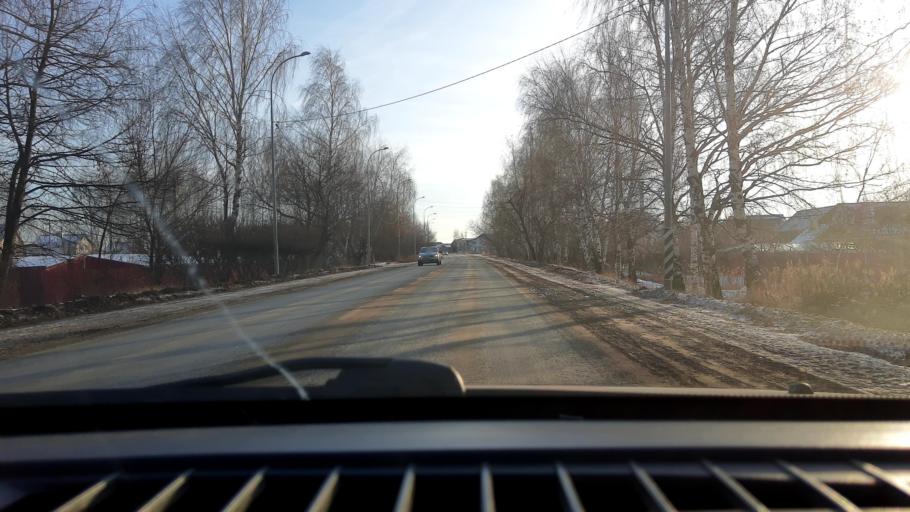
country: RU
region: Nizjnij Novgorod
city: Bor
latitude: 56.3808
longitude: 44.0400
